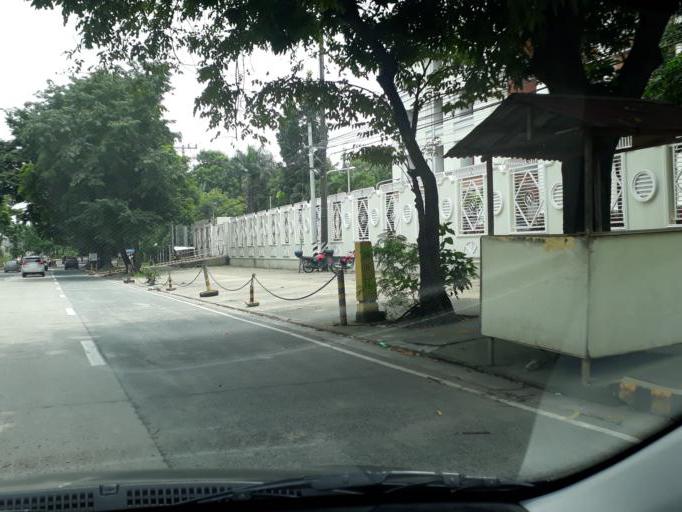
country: PH
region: Metro Manila
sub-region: Quezon City
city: Quezon City
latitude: 14.6483
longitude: 121.0399
